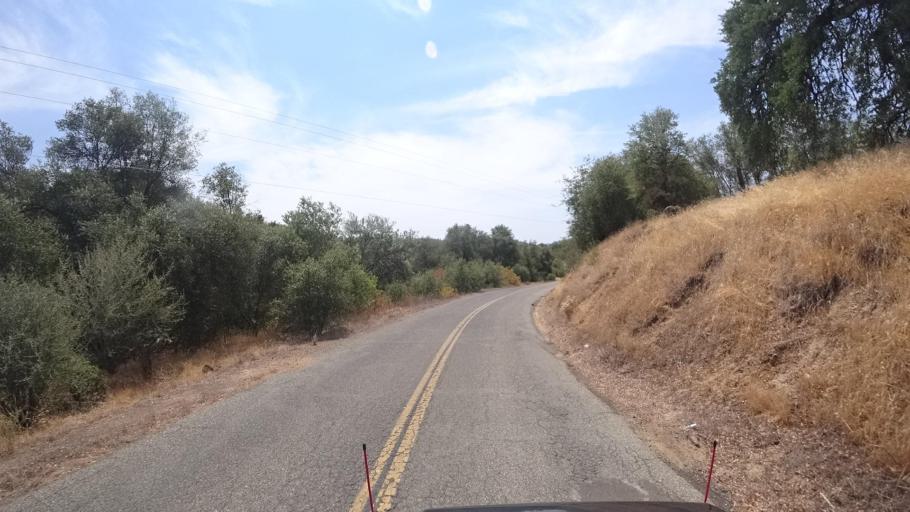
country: US
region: California
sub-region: Mariposa County
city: Mariposa
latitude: 37.4254
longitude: -119.8598
